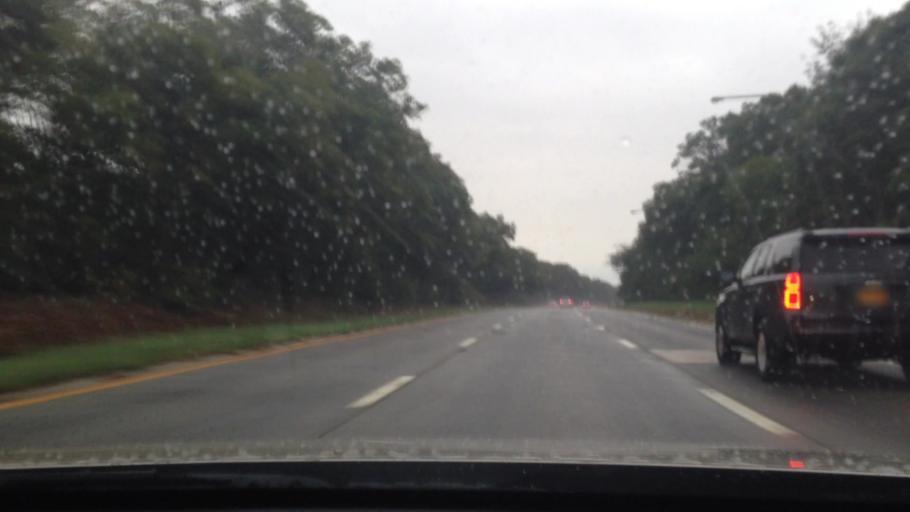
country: US
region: New York
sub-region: Suffolk County
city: Bay Shore
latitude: 40.7531
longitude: -73.2395
